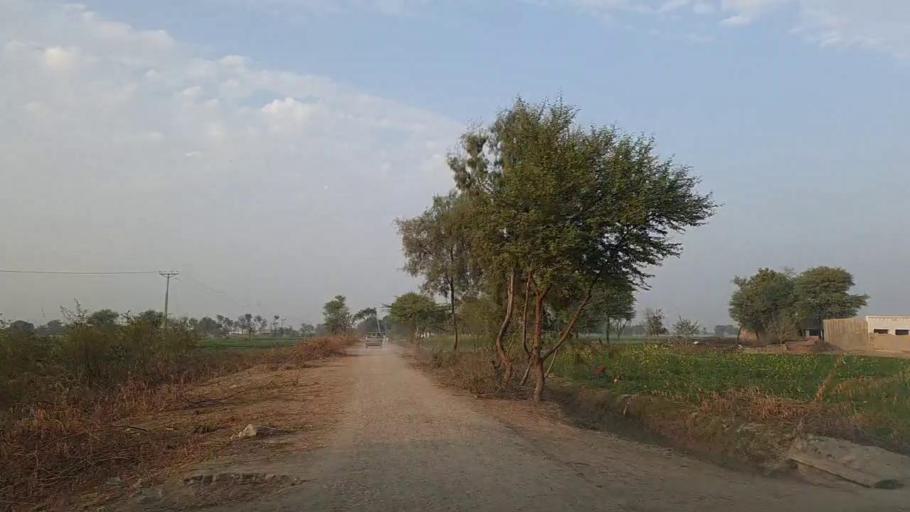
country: PK
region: Sindh
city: Jam Sahib
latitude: 26.3177
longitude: 68.6091
